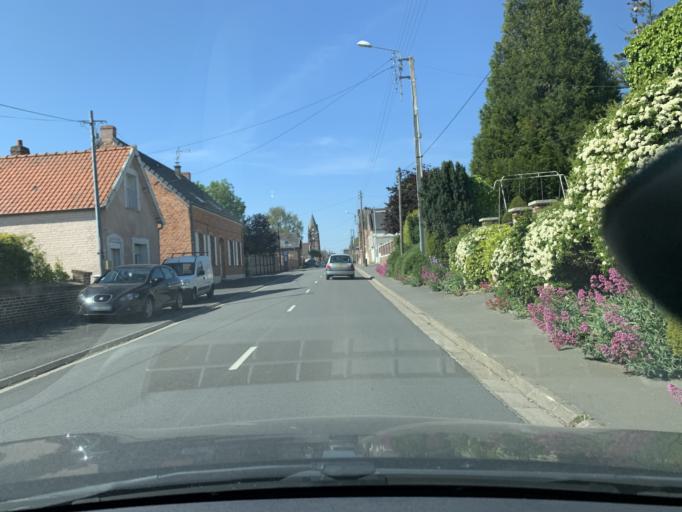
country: FR
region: Nord-Pas-de-Calais
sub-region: Departement du Nord
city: Masnieres
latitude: 50.0976
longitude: 3.2415
